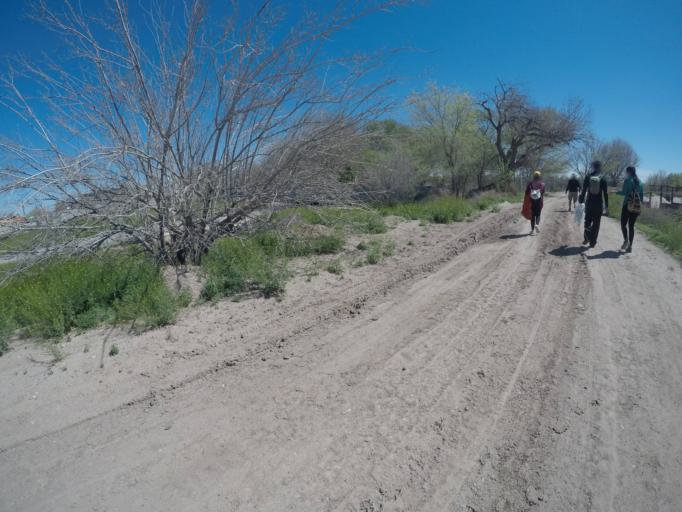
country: US
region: Texas
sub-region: El Paso County
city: Socorro Mission Number 1 Colonia
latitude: 31.6161
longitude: -106.3180
